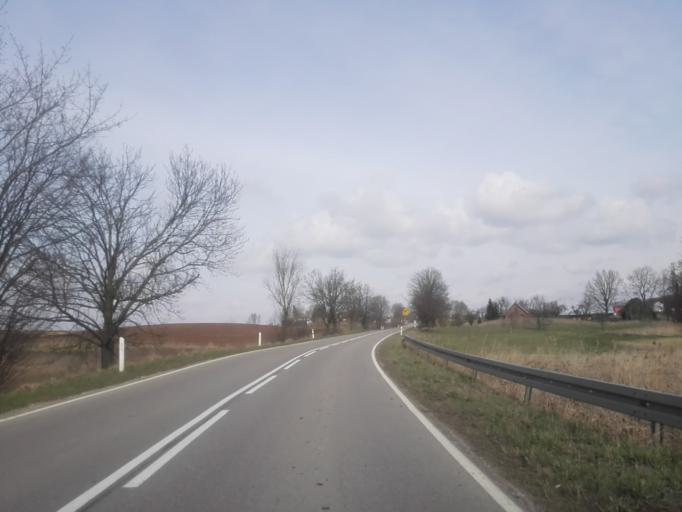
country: PL
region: Podlasie
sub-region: Powiat sejnenski
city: Sejny
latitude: 54.0863
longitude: 23.3452
